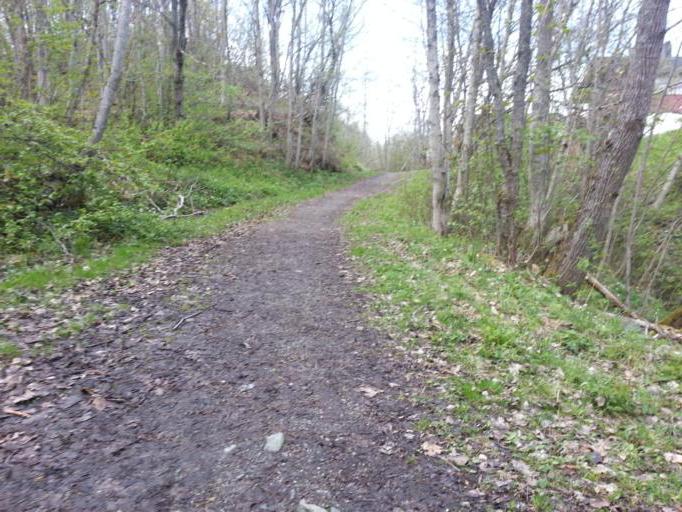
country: NO
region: Sor-Trondelag
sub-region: Trondheim
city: Trondheim
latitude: 63.3872
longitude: 10.3617
